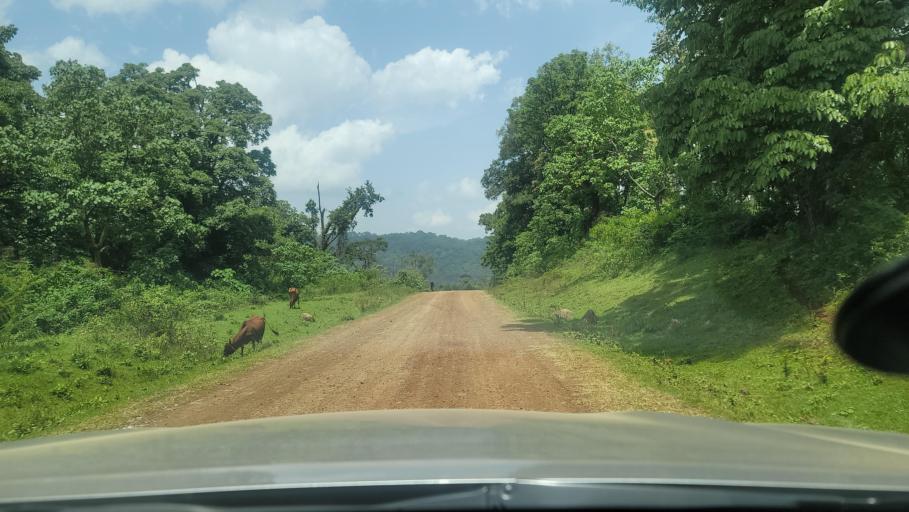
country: ET
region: Oromiya
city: Agaro
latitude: 7.7067
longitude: 36.2535
